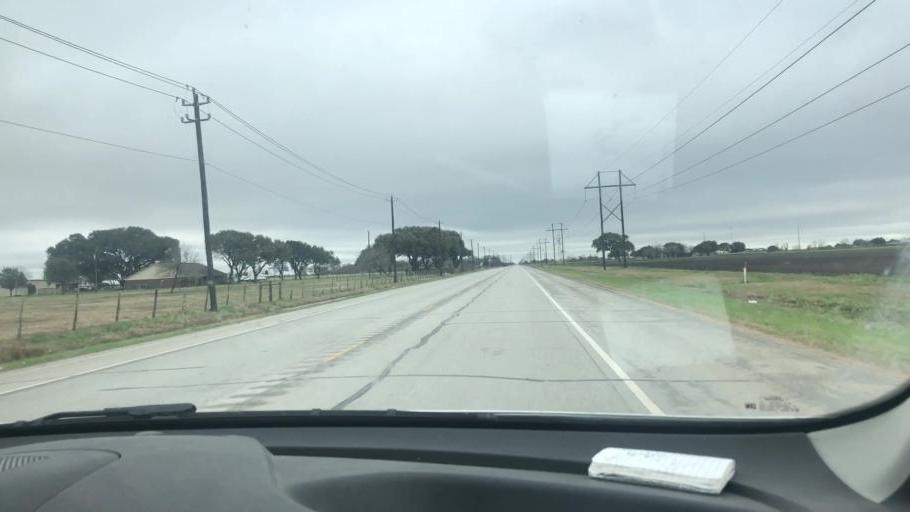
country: US
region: Texas
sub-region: Wharton County
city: Boling
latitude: 29.2045
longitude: -96.0227
